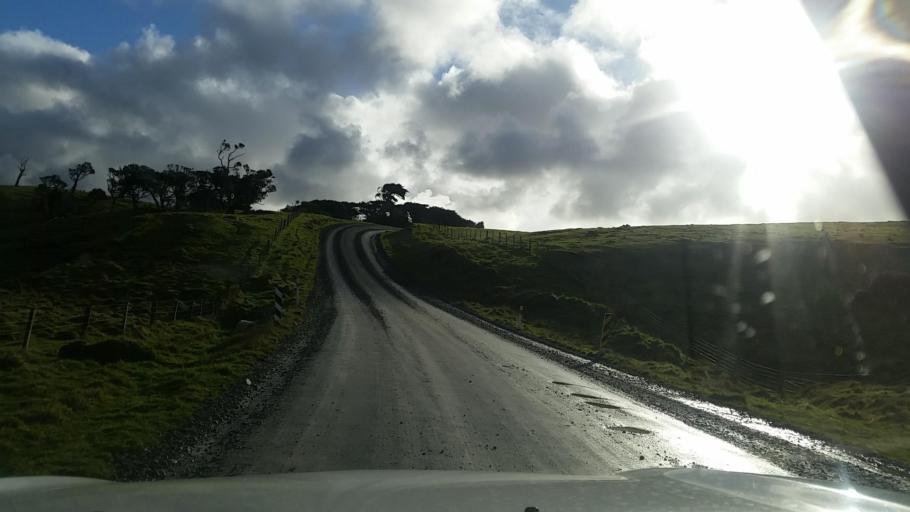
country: NZ
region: Chatham Islands
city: Waitangi
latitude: -43.8181
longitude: -176.5784
